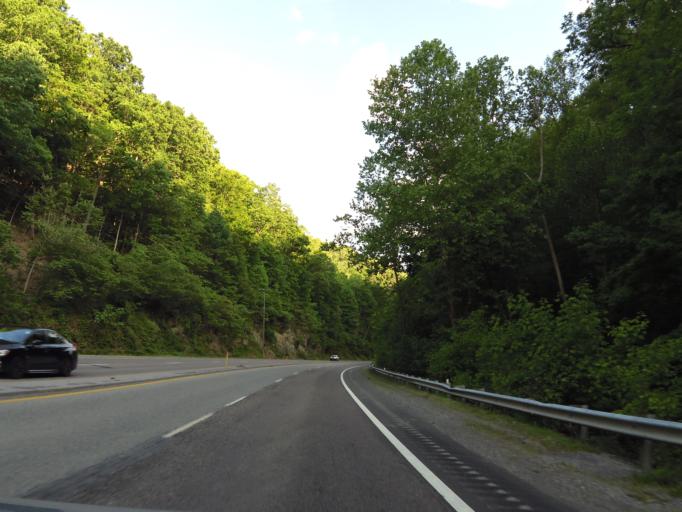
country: US
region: Virginia
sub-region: Washington County
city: Abingdon
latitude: 36.7566
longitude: -82.0585
